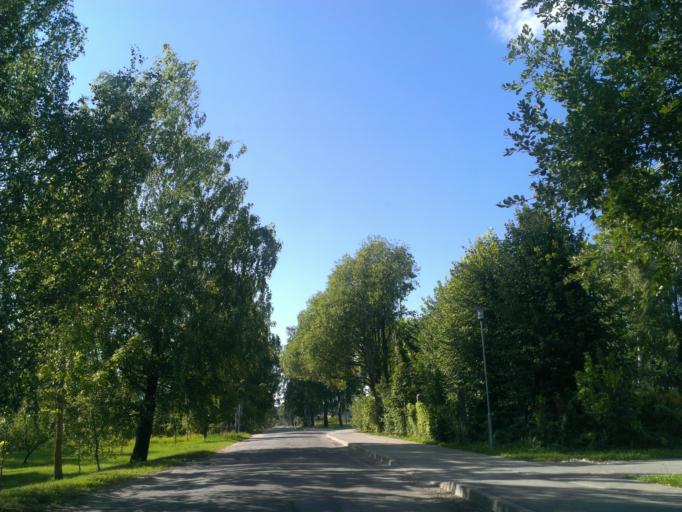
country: LV
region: Sigulda
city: Sigulda
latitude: 57.1642
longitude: 24.8778
